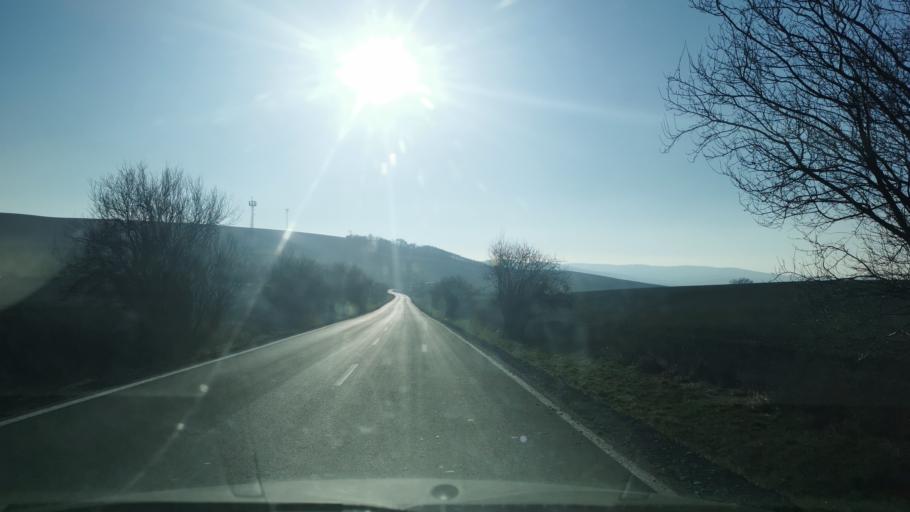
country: SK
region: Trnavsky
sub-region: Okres Senica
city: Senica
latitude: 48.7483
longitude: 17.3461
